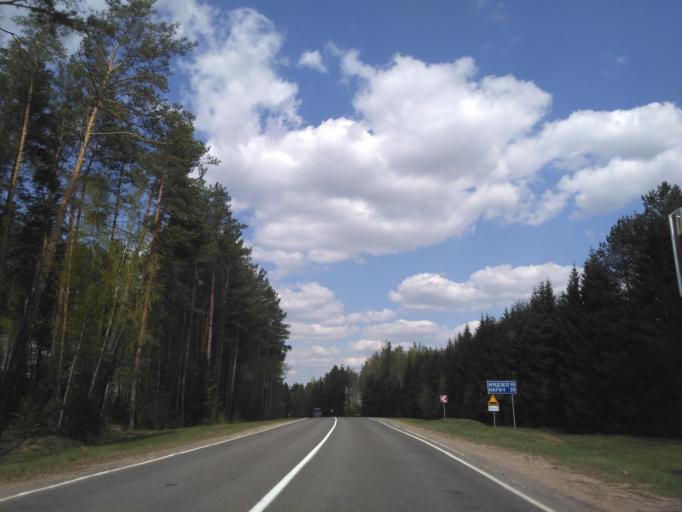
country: BY
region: Minsk
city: Myadzyel
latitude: 54.7071
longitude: 26.9337
